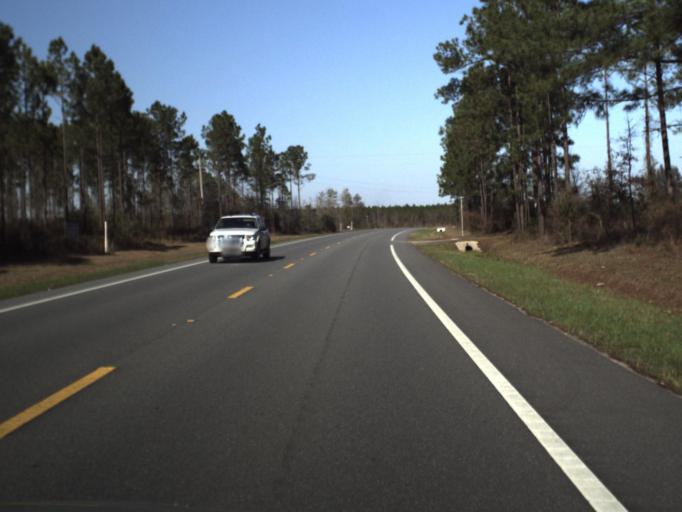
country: US
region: Florida
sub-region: Calhoun County
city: Blountstown
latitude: 30.4222
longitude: -85.1995
